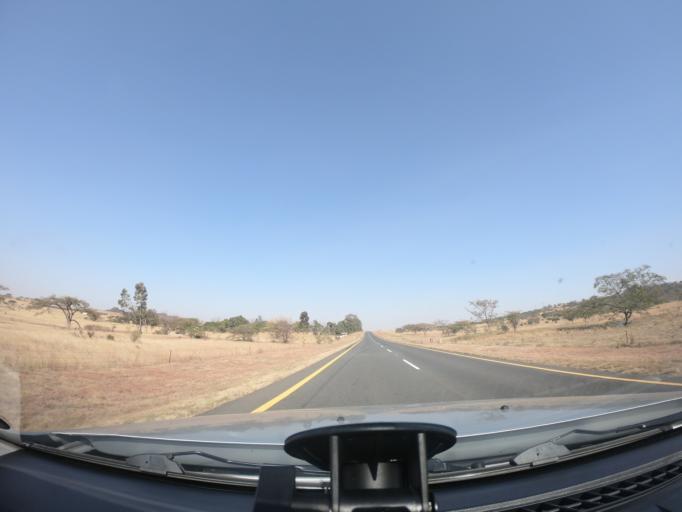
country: ZA
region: KwaZulu-Natal
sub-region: uThukela District Municipality
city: Ekuvukeni
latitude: -28.3622
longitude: 29.9564
